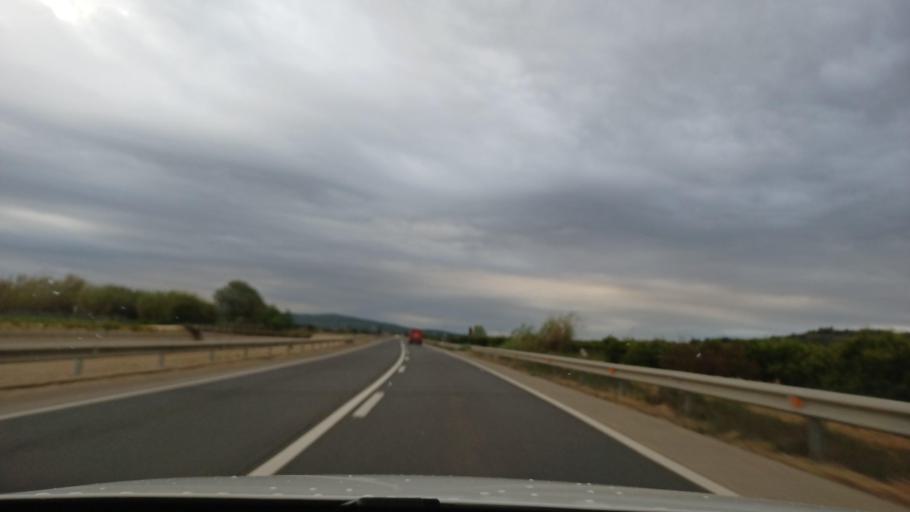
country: ES
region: Catalonia
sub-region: Provincia de Tarragona
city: Masdenverge
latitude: 40.7515
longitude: 0.5456
